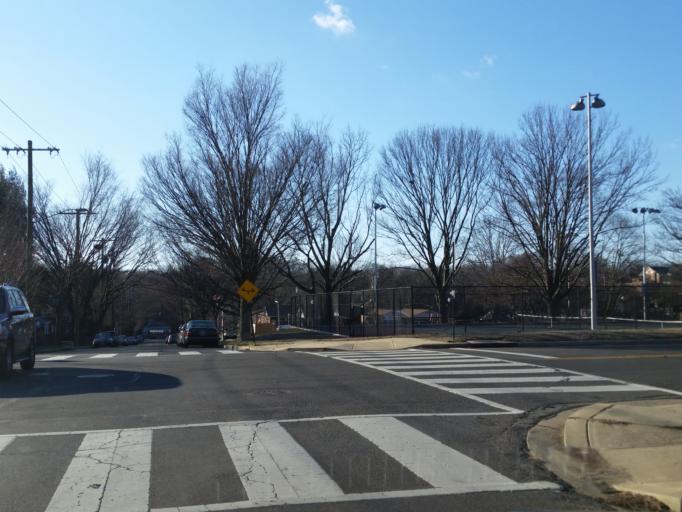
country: US
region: Maryland
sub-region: Montgomery County
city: Silver Spring
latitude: 38.9699
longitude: -77.0295
